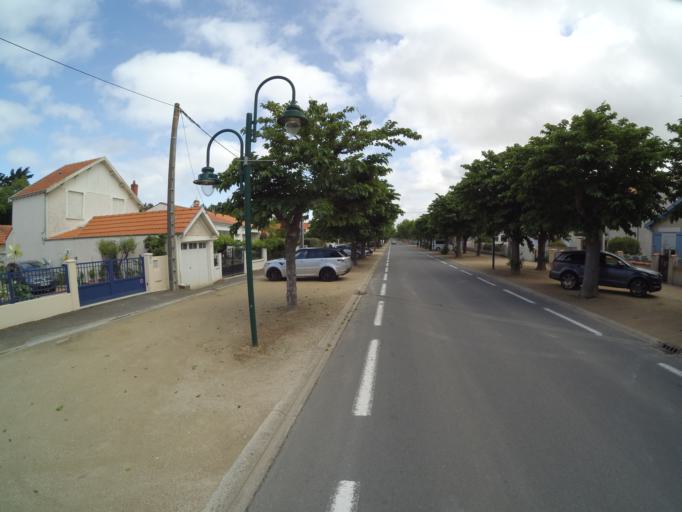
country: FR
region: Poitou-Charentes
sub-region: Departement de la Charente-Maritime
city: Chatelaillon-Plage
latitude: 46.0643
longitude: -1.0920
